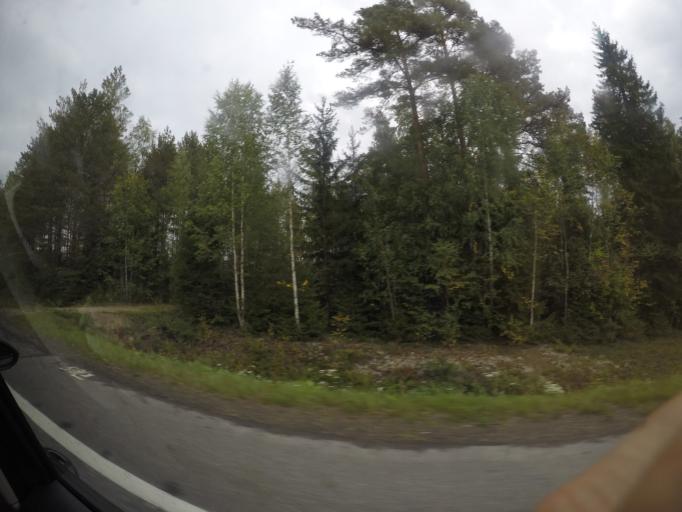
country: FI
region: Haeme
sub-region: Haemeenlinna
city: Parola
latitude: 61.1457
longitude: 24.4133
